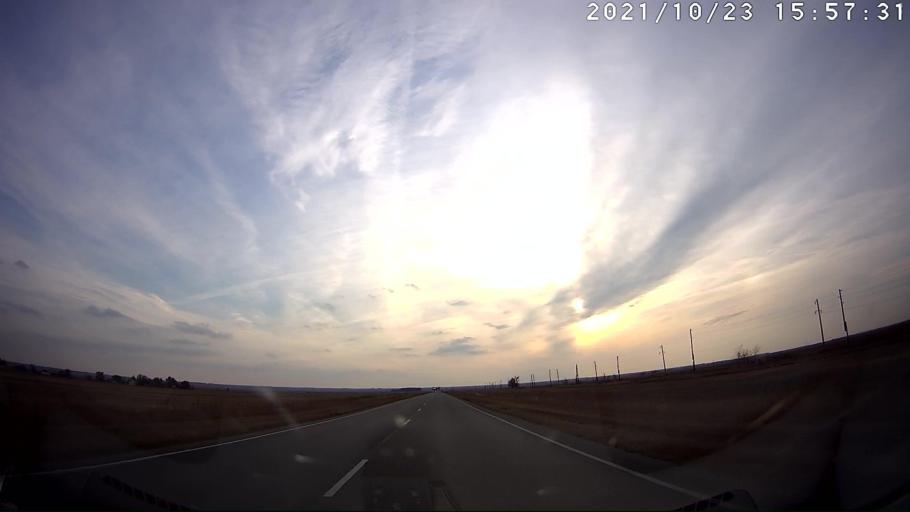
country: RU
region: Kalmykiya
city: Sadovoye
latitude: 47.9458
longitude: 43.9315
